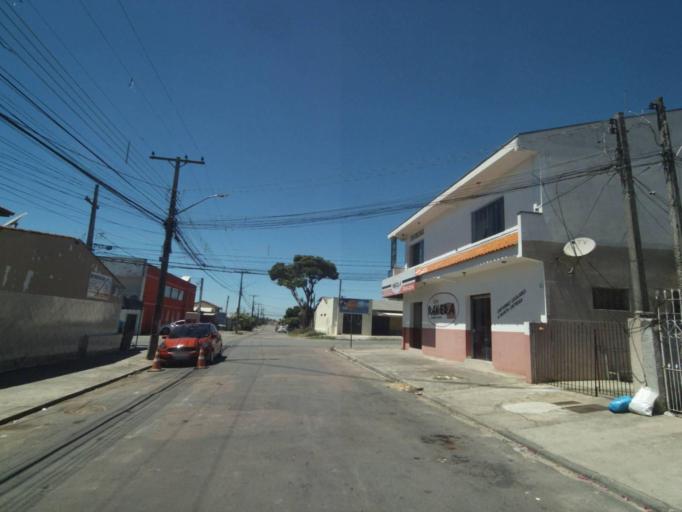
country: BR
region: Parana
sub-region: Curitiba
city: Curitiba
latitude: -25.4766
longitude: -49.3480
